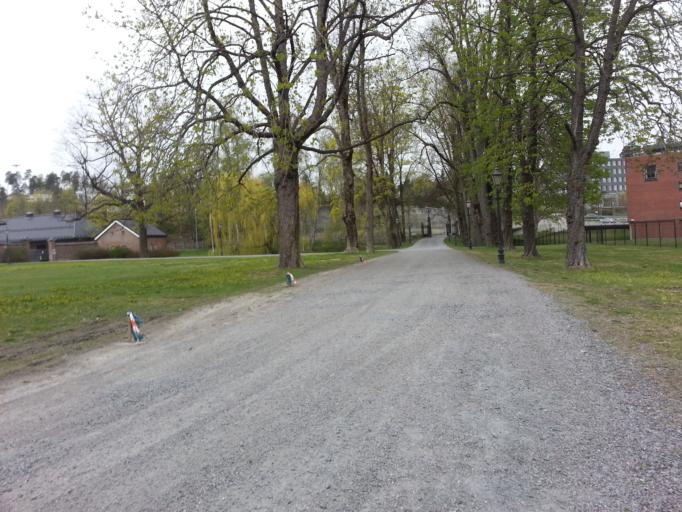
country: NO
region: Akershus
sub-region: Baerum
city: Lysaker
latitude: 59.9145
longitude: 10.6564
